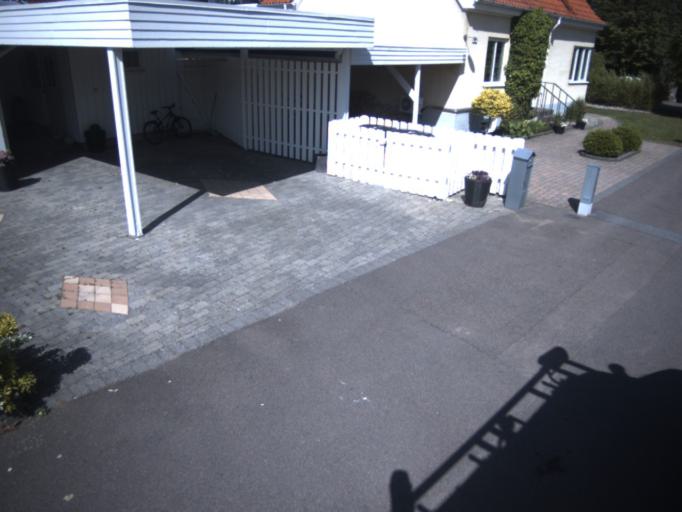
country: DK
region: Capital Region
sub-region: Helsingor Kommune
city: Helsingor
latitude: 56.0990
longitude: 12.6407
